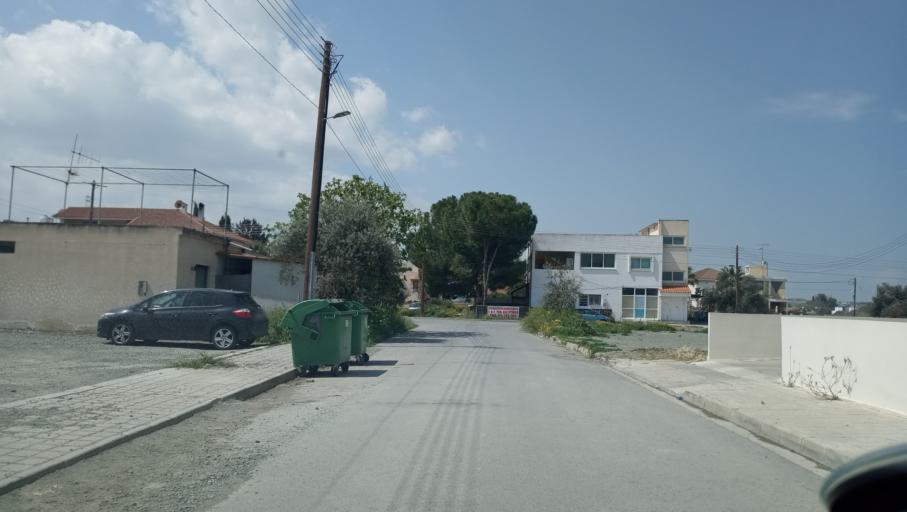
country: CY
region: Lefkosia
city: Dali
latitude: 35.0182
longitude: 33.4105
